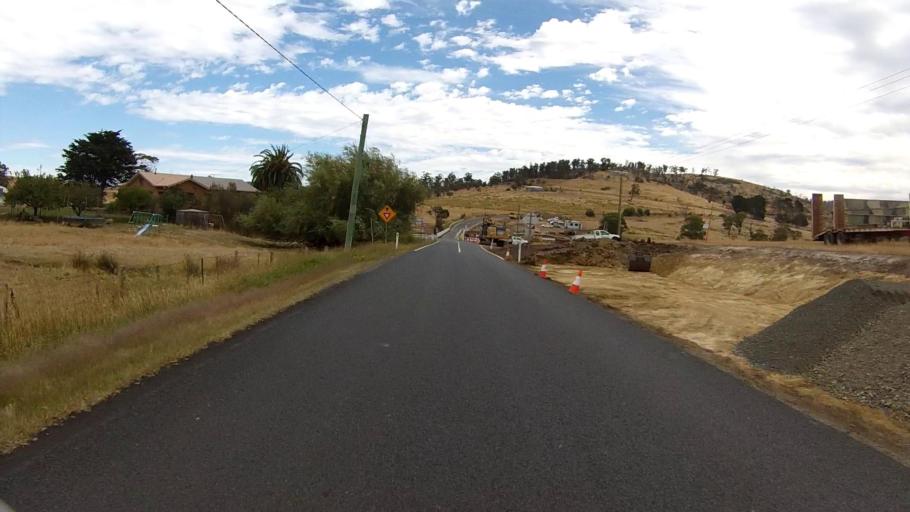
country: AU
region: Tasmania
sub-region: Sorell
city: Sorell
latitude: -42.8725
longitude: 147.7020
